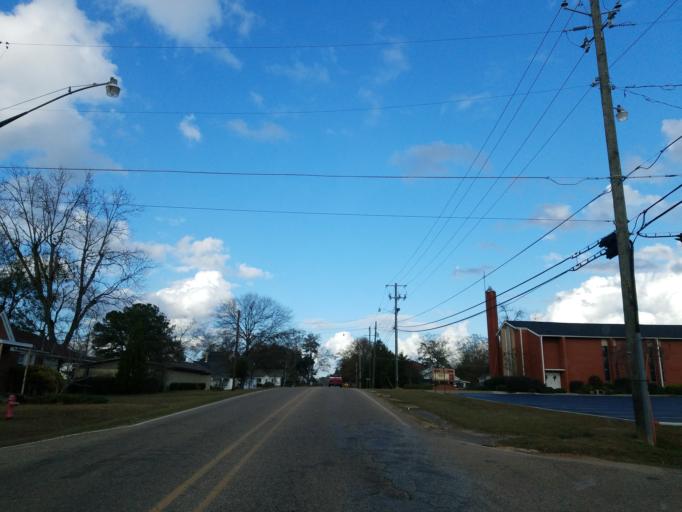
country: US
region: Mississippi
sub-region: Jones County
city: Ellisville
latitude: 31.6016
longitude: -89.1952
